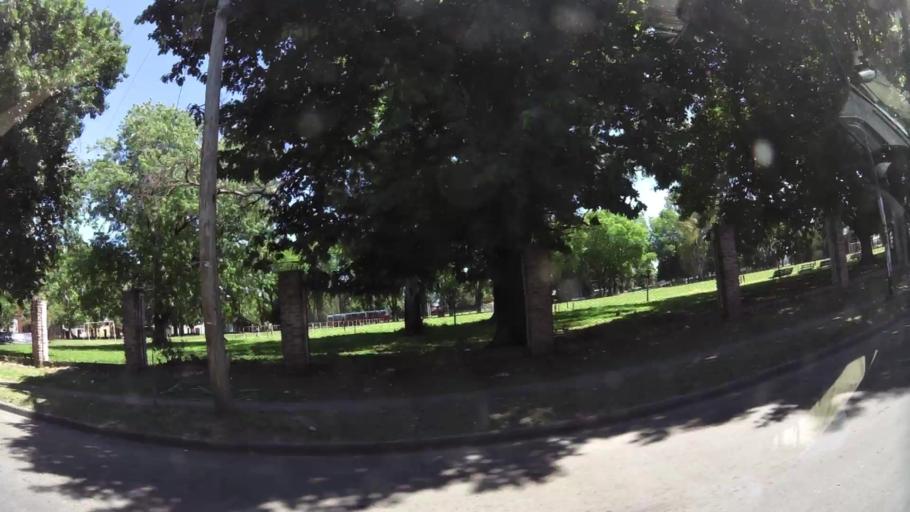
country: AR
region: Buenos Aires
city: Caseros
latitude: -34.5774
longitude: -58.5575
